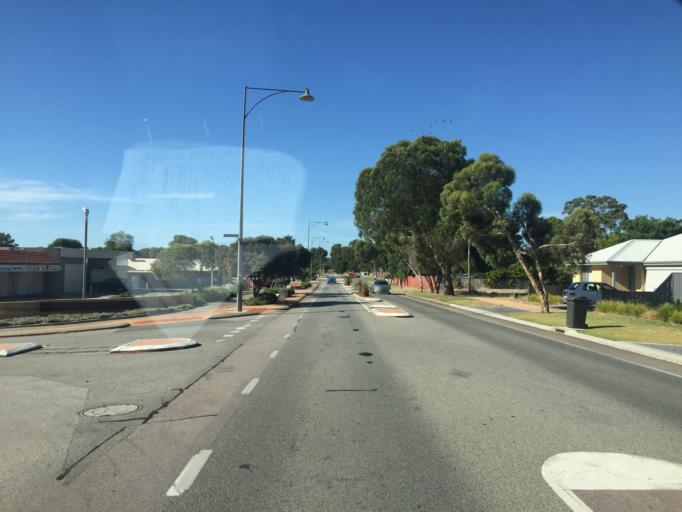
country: AU
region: Western Australia
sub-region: Gosnells
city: Maddington
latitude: -32.0348
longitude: 115.9822
